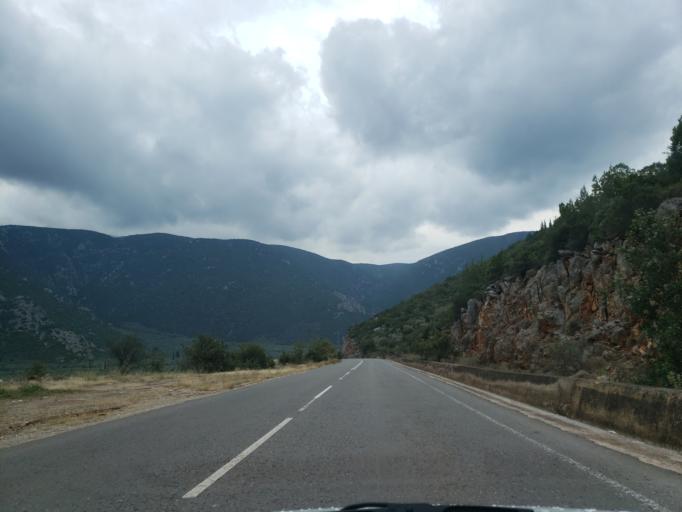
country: GR
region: Central Greece
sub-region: Nomos Fokidos
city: Amfissa
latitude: 38.5423
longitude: 22.4107
